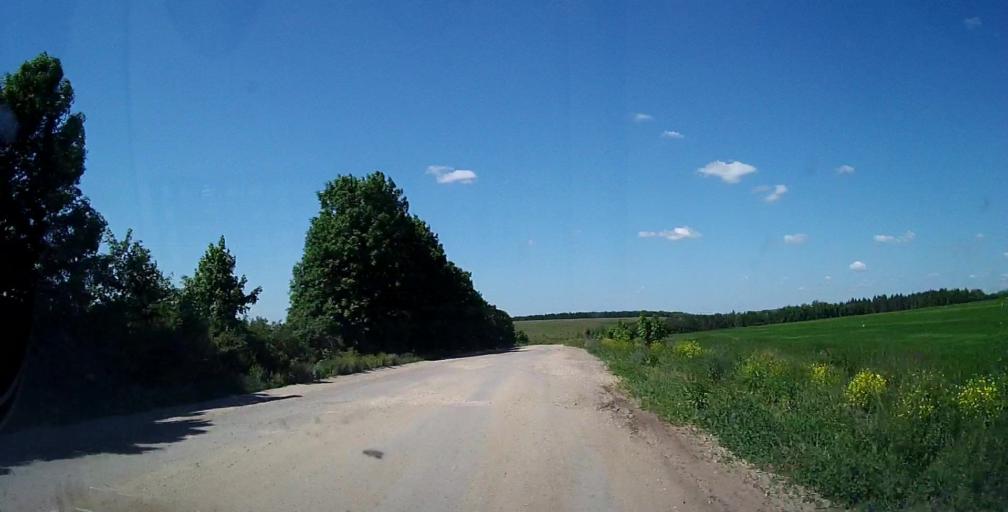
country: RU
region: Tula
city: Kurkino
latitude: 53.2004
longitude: 38.5838
